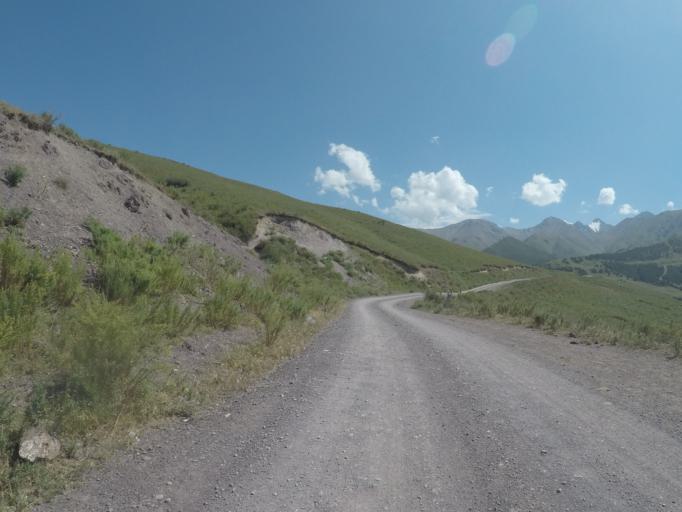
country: KG
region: Chuy
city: Bishkek
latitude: 42.6503
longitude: 74.5205
